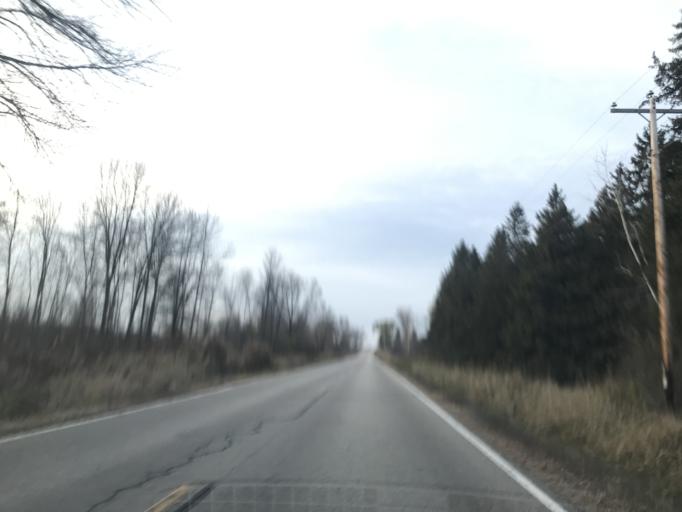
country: US
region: Wisconsin
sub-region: Marinette County
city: Peshtigo
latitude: 45.1035
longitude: -87.7994
